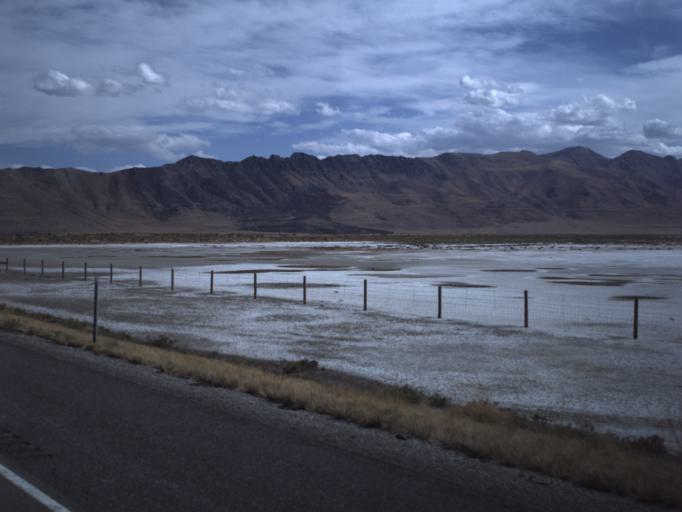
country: US
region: Utah
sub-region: Tooele County
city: Grantsville
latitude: 40.7498
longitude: -112.6944
